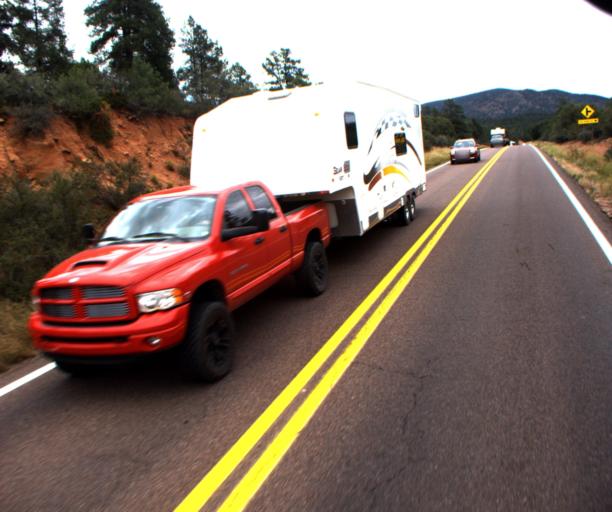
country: US
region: Arizona
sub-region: Gila County
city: Star Valley
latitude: 34.2630
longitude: -111.2168
